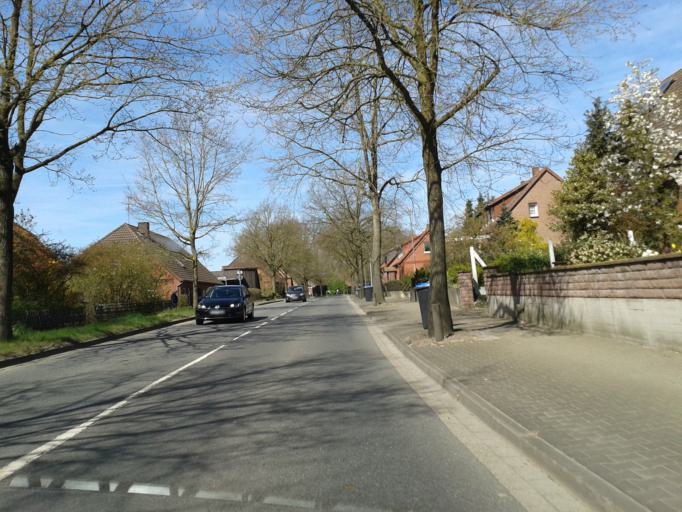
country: DE
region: Lower Saxony
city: Suderburg
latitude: 52.9541
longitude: 10.4825
